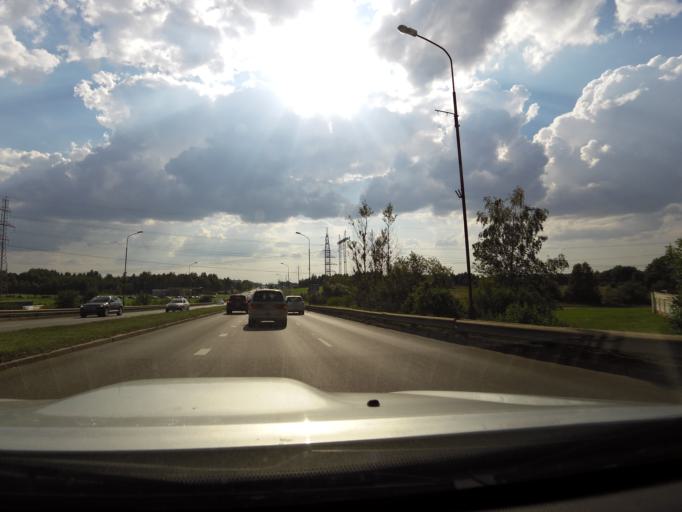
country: LT
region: Siauliu apskritis
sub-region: Siauliai
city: Siauliai
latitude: 55.9264
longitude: 23.2830
